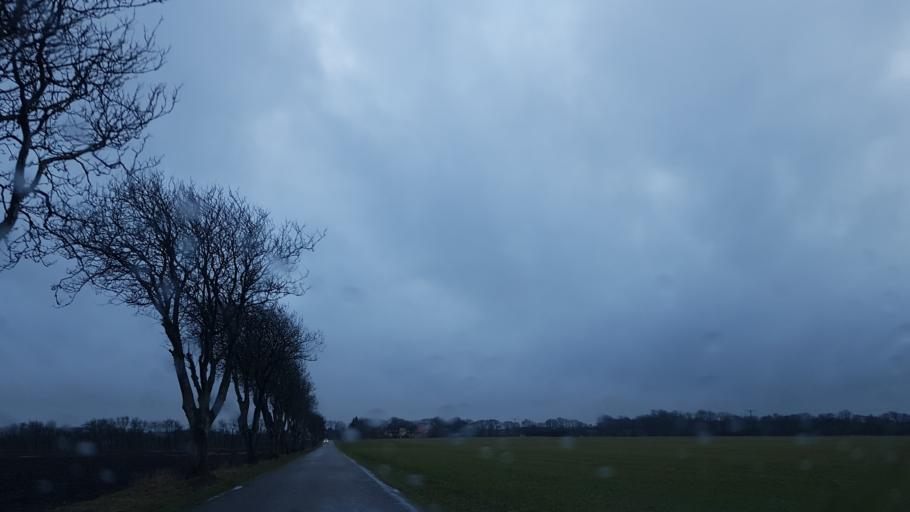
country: DK
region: South Denmark
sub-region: Vejen Kommune
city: Rodding
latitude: 55.3326
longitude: 9.1856
